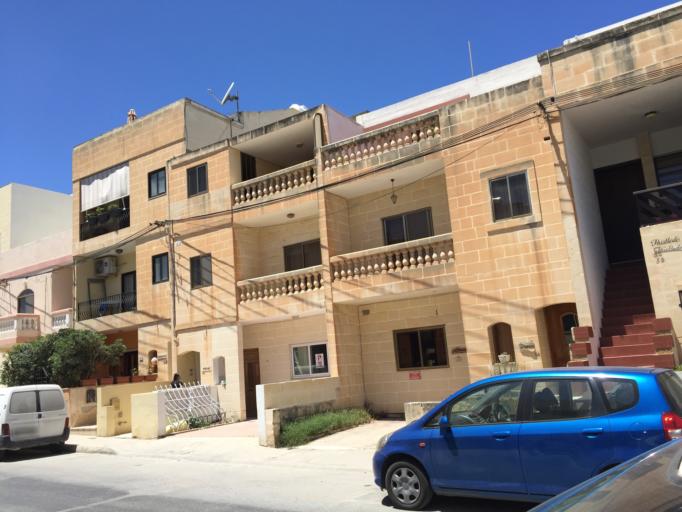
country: MT
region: Is-Swieqi
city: Swieqi
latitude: 35.9201
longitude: 14.4817
